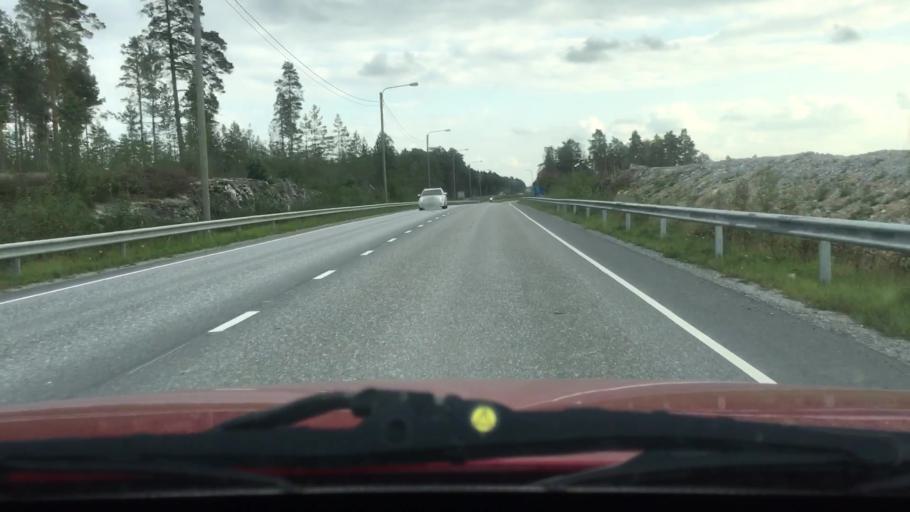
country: FI
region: Varsinais-Suomi
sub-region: Turku
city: Masku
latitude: 60.5463
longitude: 22.1273
